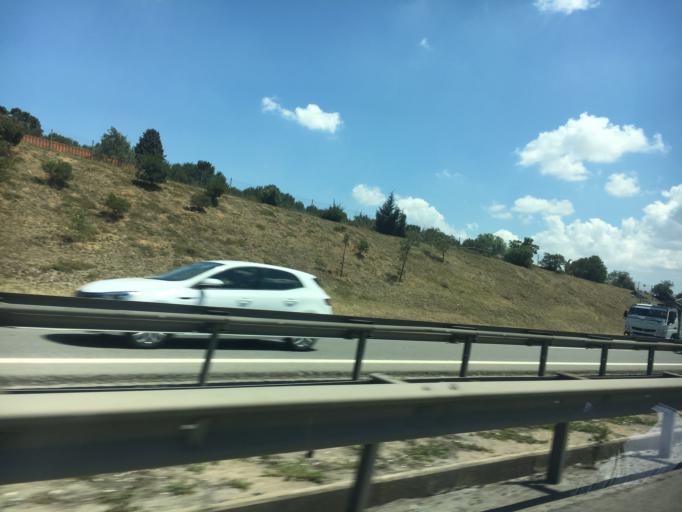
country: TR
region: Kocaeli
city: Balcik
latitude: 40.8912
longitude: 29.3718
